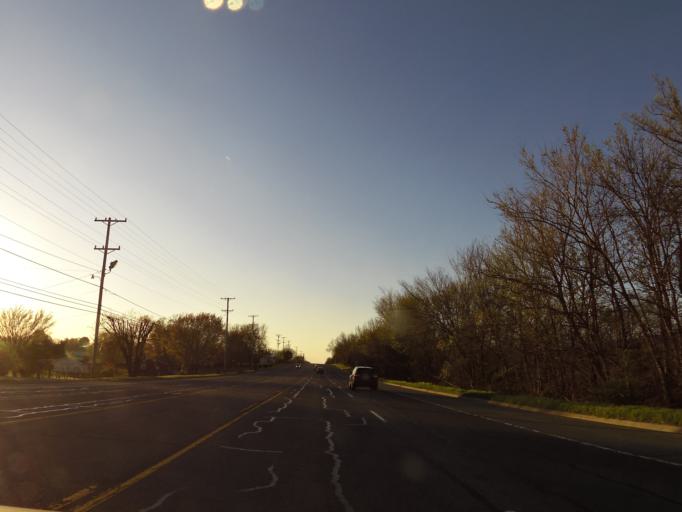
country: US
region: Tennessee
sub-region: Robertson County
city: Greenbrier
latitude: 36.4469
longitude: -86.8164
